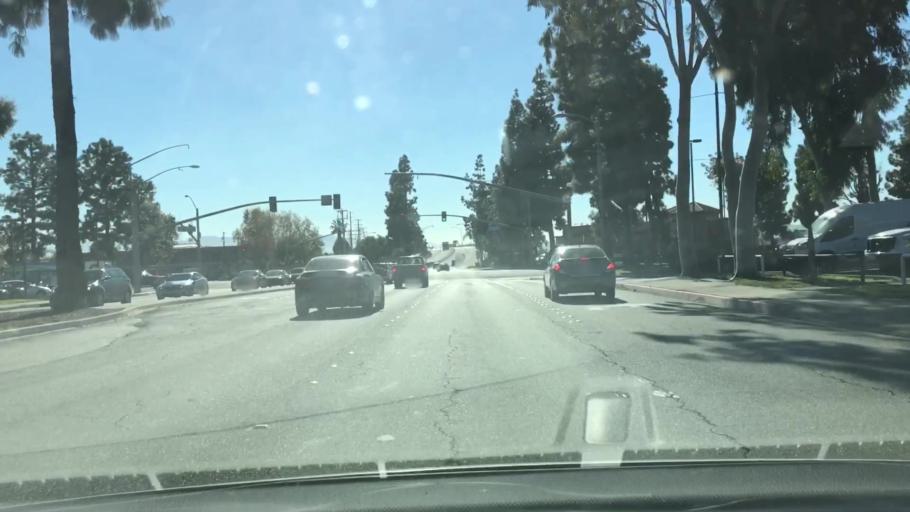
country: US
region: California
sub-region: San Bernardino County
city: Montclair
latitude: 34.0640
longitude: -117.6897
